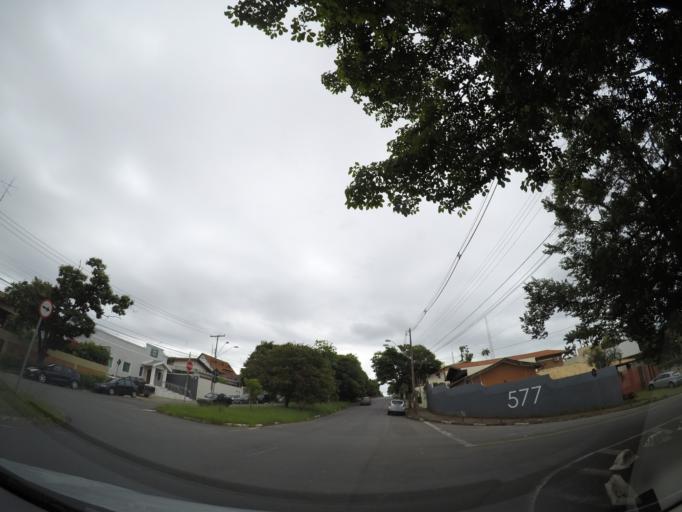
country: BR
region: Sao Paulo
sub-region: Campinas
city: Campinas
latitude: -22.9093
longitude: -47.0344
